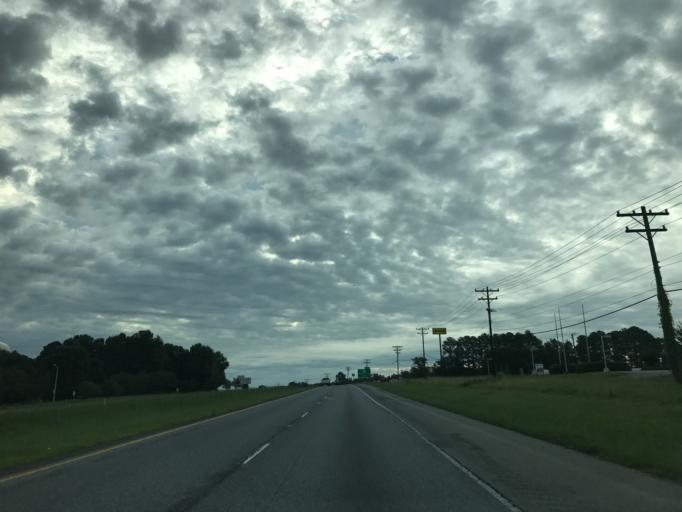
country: US
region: South Carolina
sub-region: Spartanburg County
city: Southern Shops
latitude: 34.9727
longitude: -81.9899
